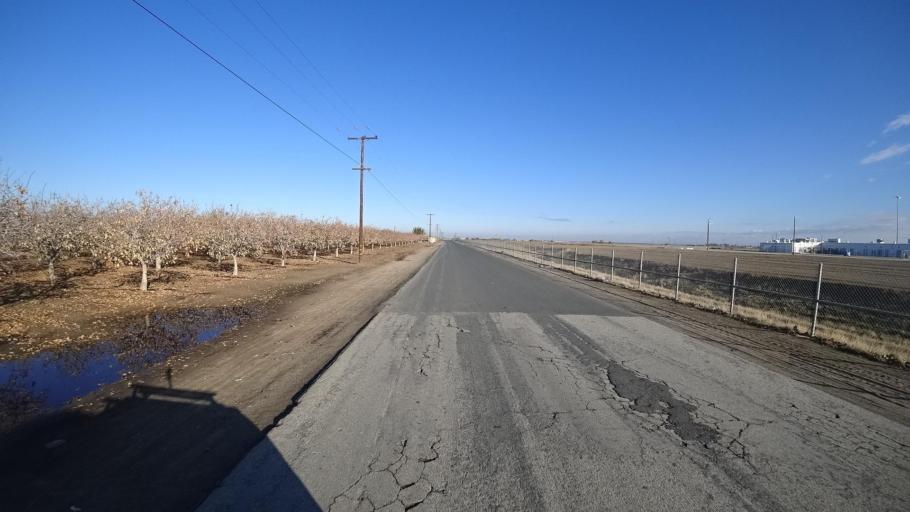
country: US
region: California
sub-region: Kern County
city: Delano
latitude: 35.7710
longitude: -119.3299
